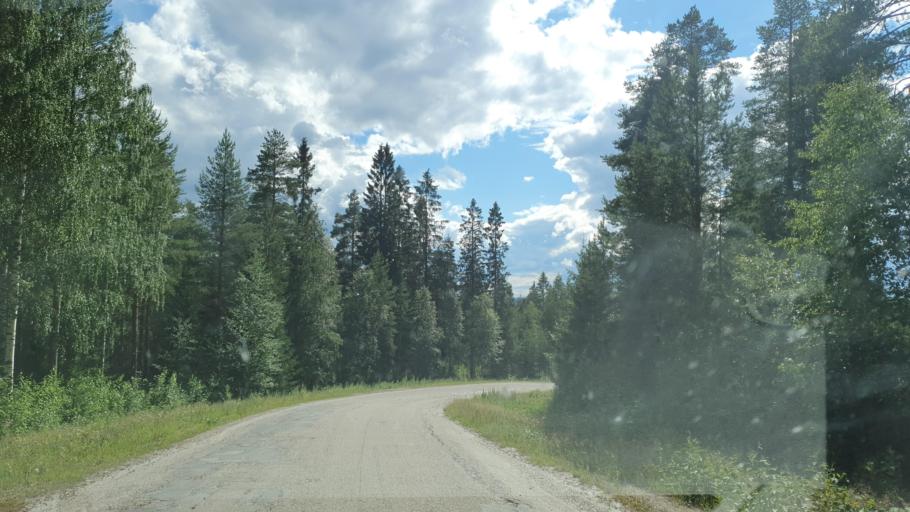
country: FI
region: Kainuu
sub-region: Kehys-Kainuu
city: Kuhmo
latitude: 64.1262
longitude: 29.6420
